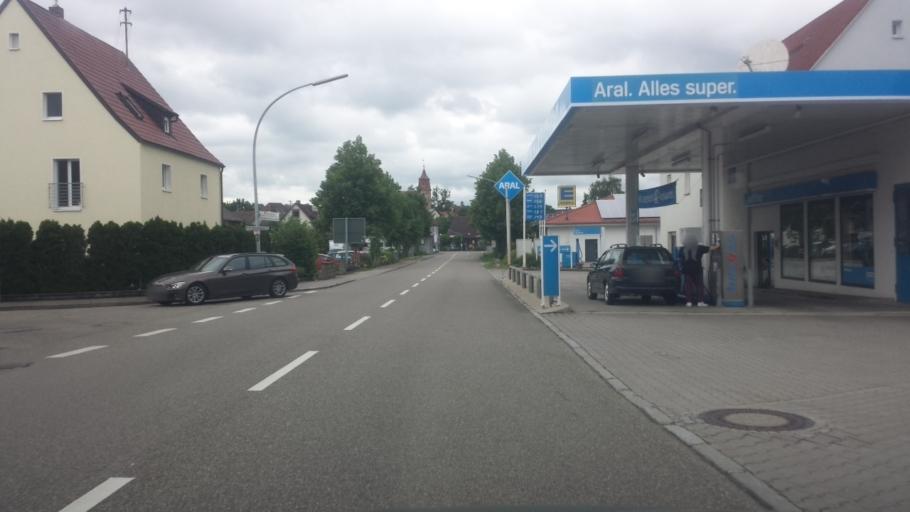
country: DE
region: Baden-Wuerttemberg
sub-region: Regierungsbezirk Stuttgart
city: Rot am See
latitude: 49.2469
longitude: 10.0286
